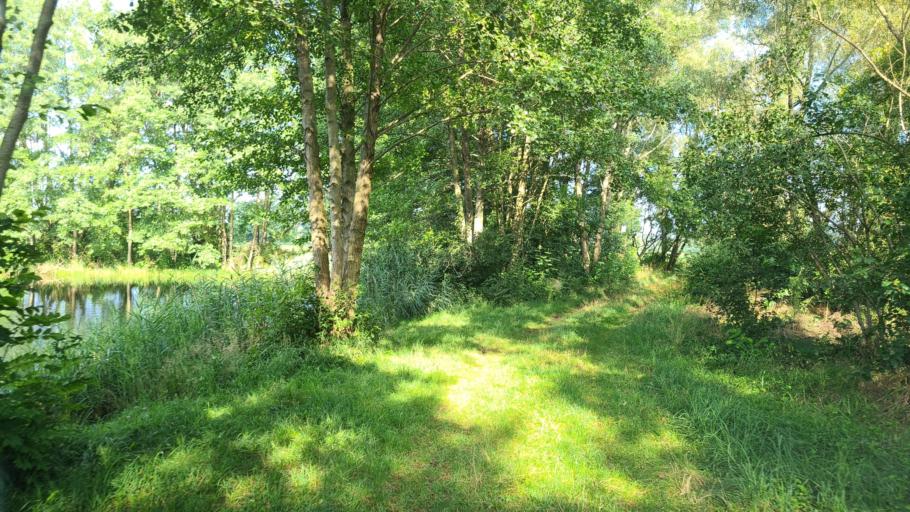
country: DE
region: Brandenburg
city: Finsterwalde
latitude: 51.6564
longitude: 13.7293
